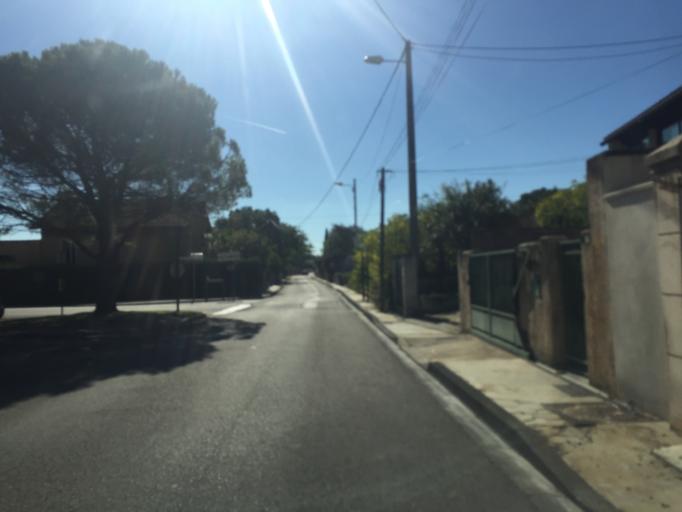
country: FR
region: Provence-Alpes-Cote d'Azur
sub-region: Departement du Vaucluse
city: Vedene
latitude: 43.9714
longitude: 4.9000
